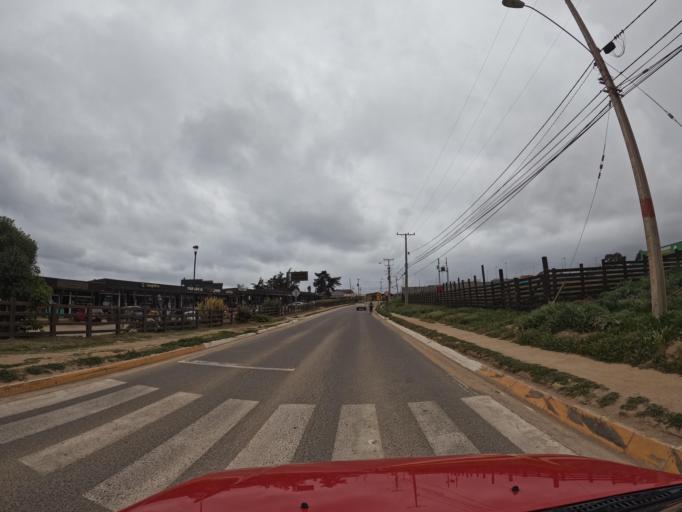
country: CL
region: O'Higgins
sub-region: Provincia de Colchagua
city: Santa Cruz
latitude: -34.4062
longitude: -72.0256
